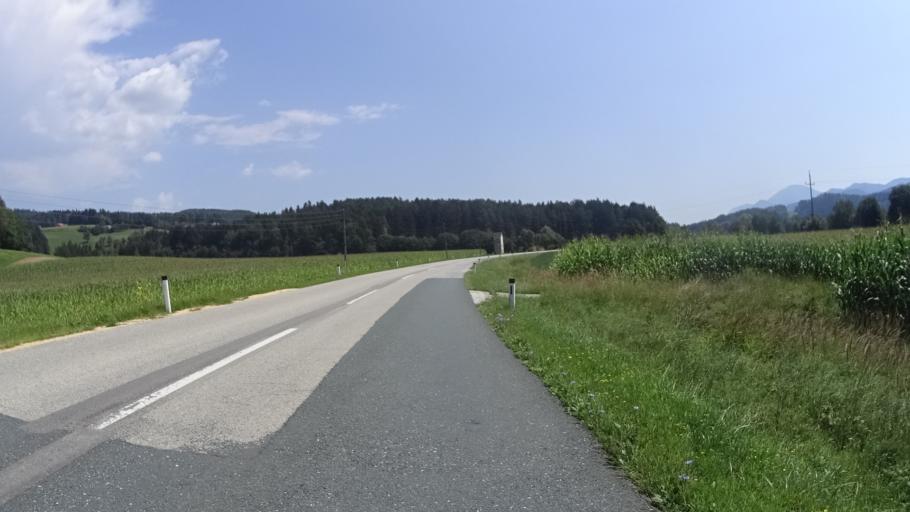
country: AT
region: Carinthia
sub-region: Politischer Bezirk Volkermarkt
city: Bleiburg/Pliberk
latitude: 46.5697
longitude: 14.8271
